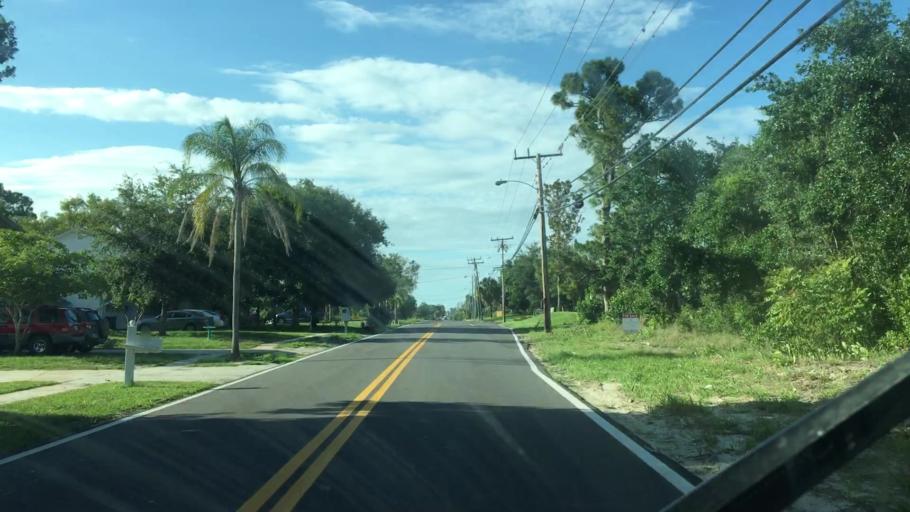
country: US
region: Florida
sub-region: Brevard County
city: Mims
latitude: 28.6235
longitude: -80.8603
